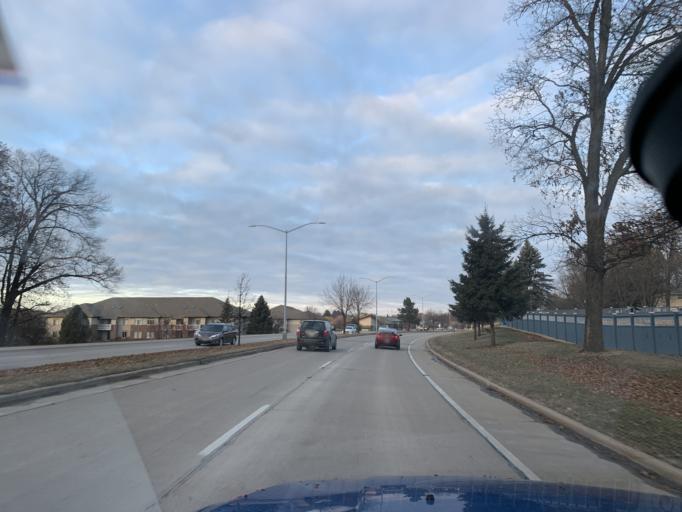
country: US
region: Wisconsin
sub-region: Dane County
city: Fitchburg
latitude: 43.0107
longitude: -89.4285
